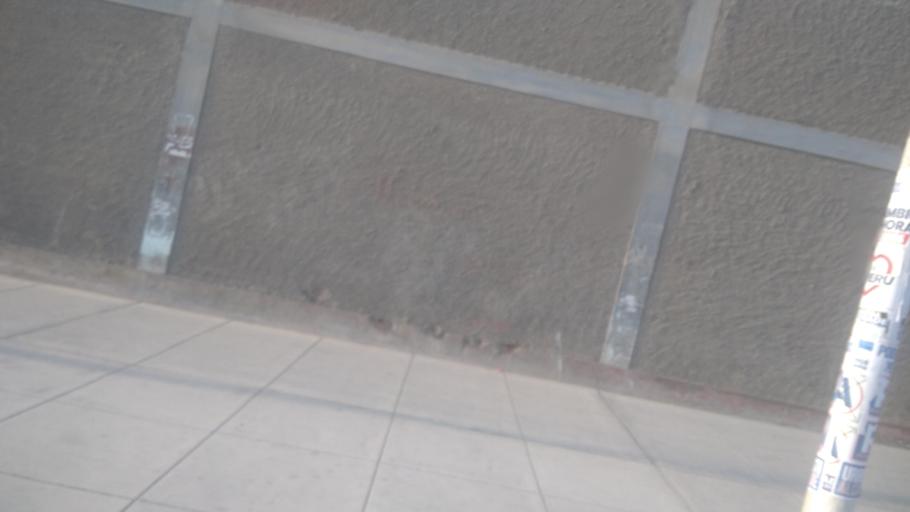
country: PE
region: Lima
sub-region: Lima
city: Vitarte
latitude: -12.0204
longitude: -76.9563
